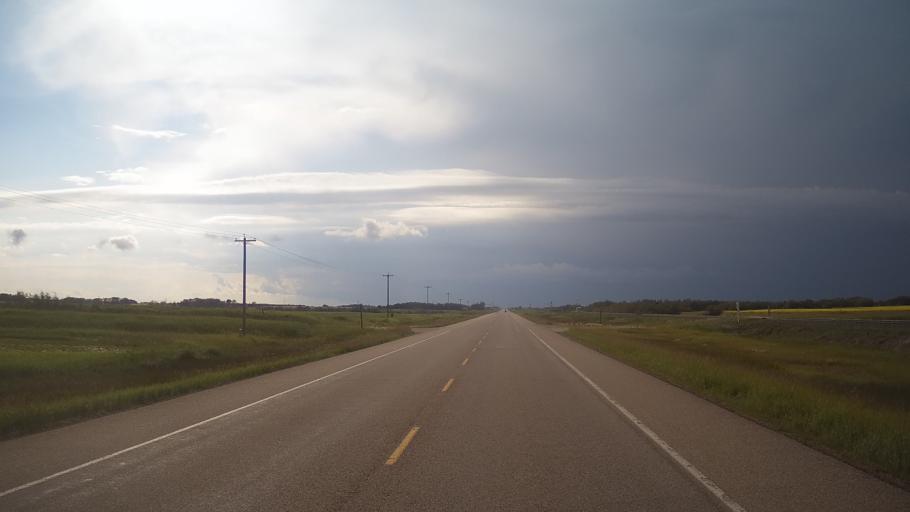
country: CA
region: Alberta
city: Viking
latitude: 53.1815
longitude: -112.0738
